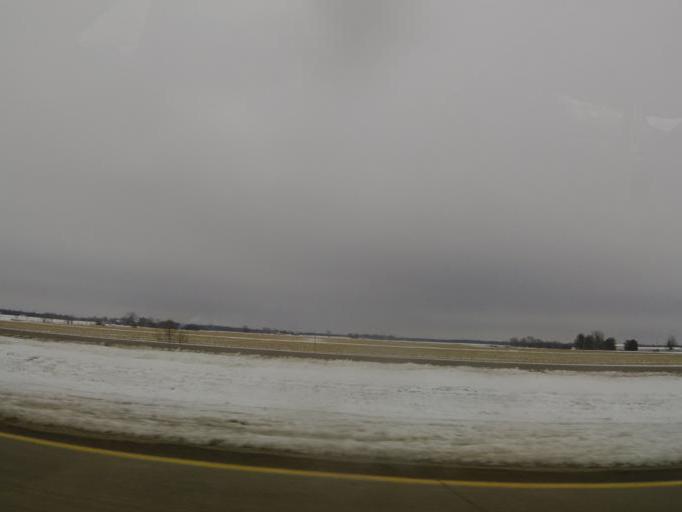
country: US
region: Illinois
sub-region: Hancock County
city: Nauvoo
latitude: 40.6268
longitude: -91.5579
